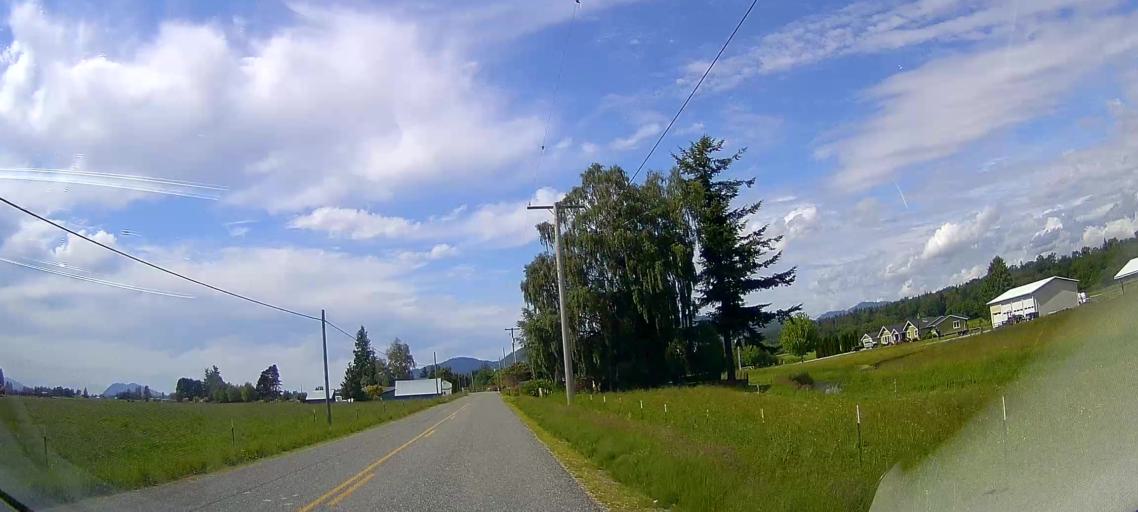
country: US
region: Washington
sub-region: Skagit County
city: Burlington
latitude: 48.5421
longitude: -122.3915
